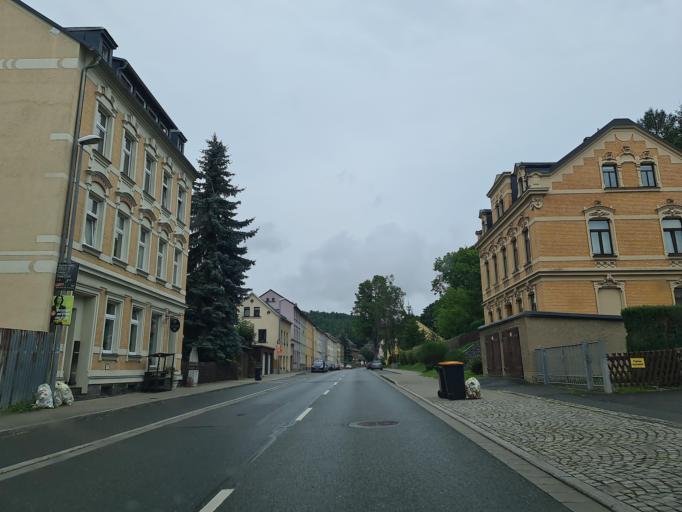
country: DE
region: Saxony
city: Oelsnitz
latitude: 50.4199
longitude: 12.1803
